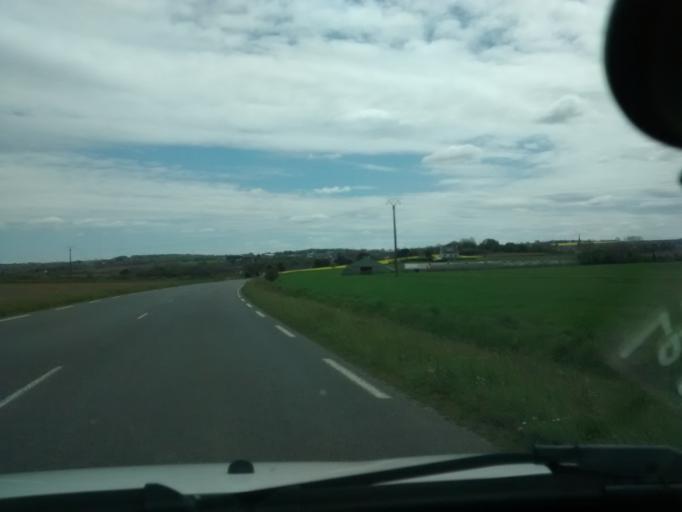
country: FR
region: Brittany
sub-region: Departement des Cotes-d'Armor
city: Langoat
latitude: 48.7567
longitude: -3.2718
